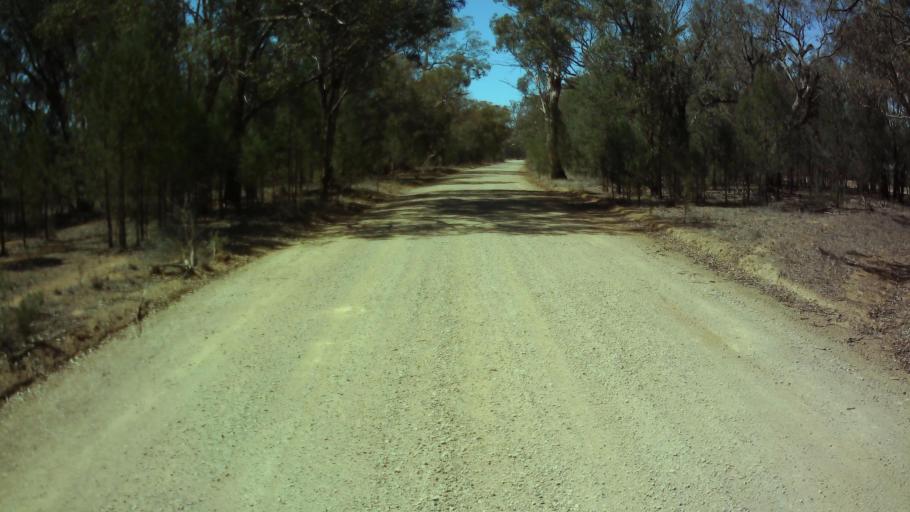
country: AU
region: New South Wales
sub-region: Weddin
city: Grenfell
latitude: -33.8616
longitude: 148.0874
